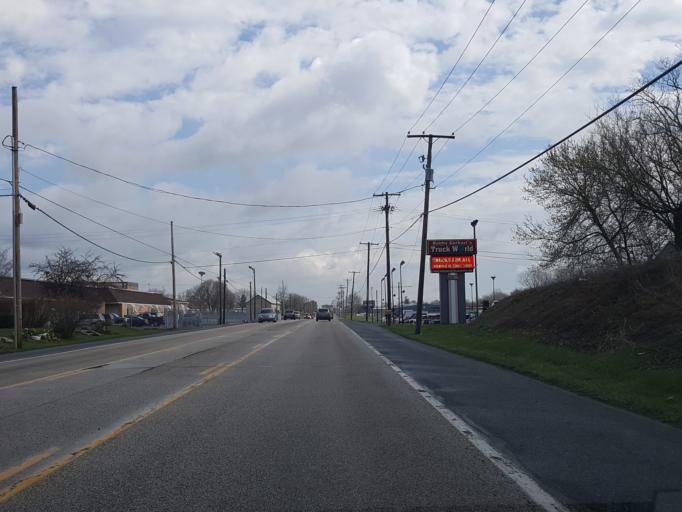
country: US
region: Pennsylvania
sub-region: Lebanon County
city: Avon
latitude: 40.3562
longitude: -76.3689
